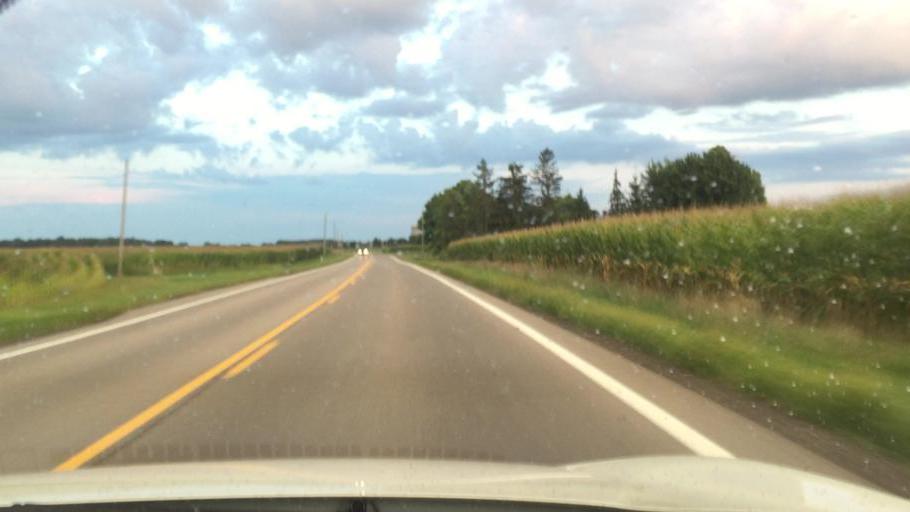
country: US
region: Ohio
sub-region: Champaign County
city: Mechanicsburg
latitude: 40.0626
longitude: -83.5432
